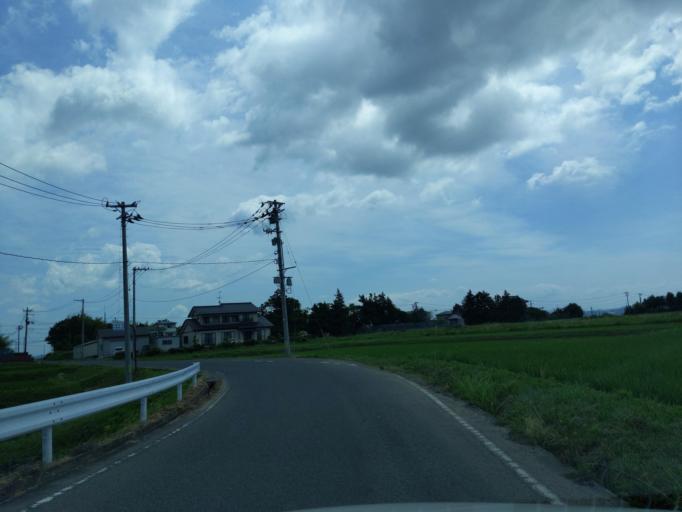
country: JP
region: Fukushima
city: Koriyama
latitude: 37.4409
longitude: 140.3564
